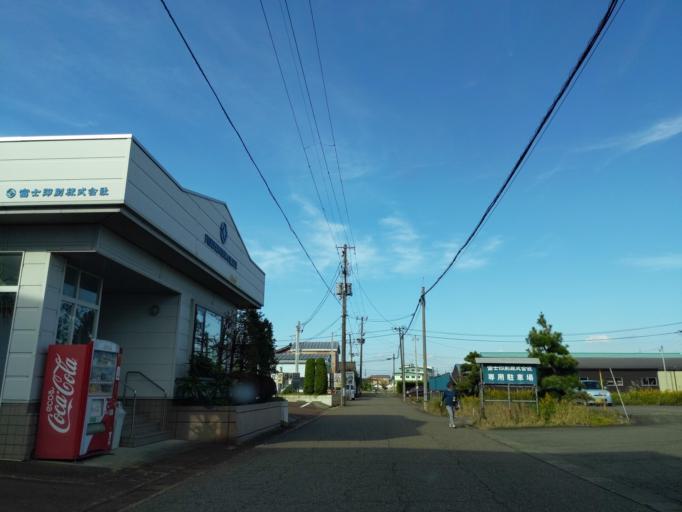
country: JP
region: Niigata
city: Sanjo
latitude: 37.6141
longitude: 138.9440
